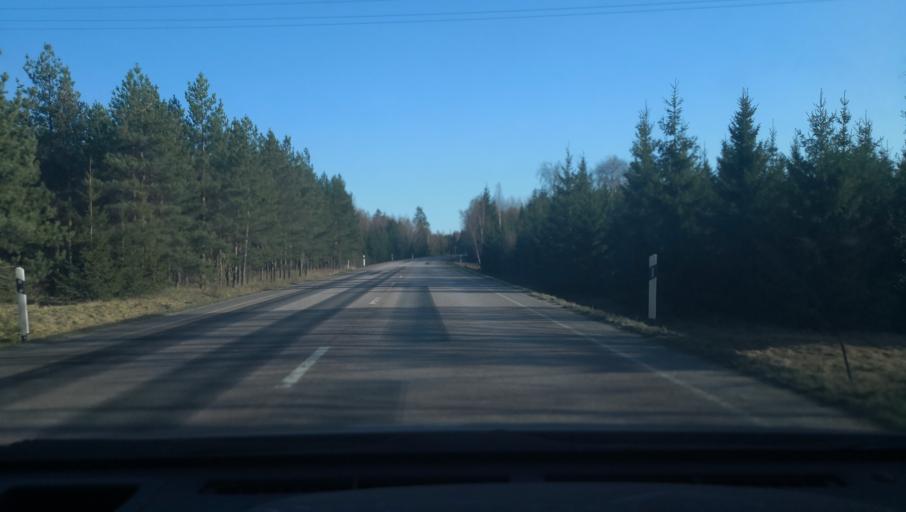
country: SE
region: Uppsala
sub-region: Heby Kommun
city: Heby
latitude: 59.9799
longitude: 16.8354
